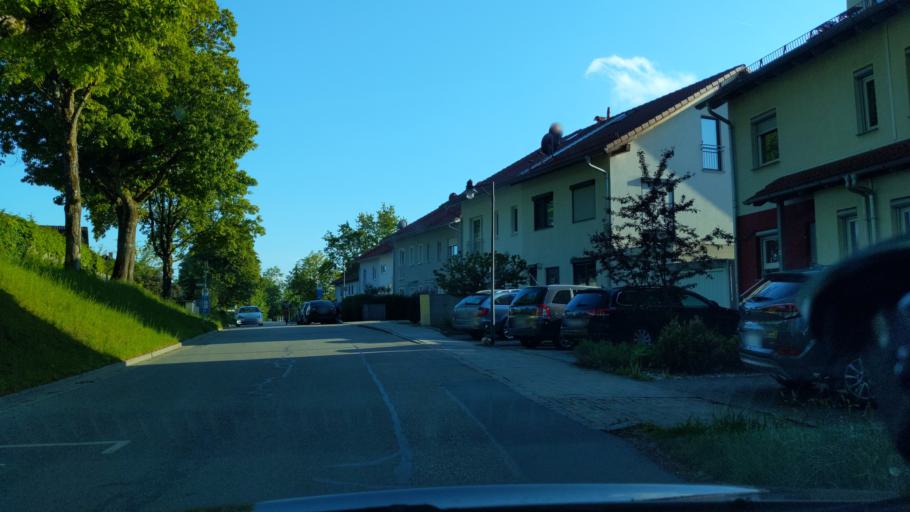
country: DE
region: Bavaria
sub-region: Upper Bavaria
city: Ebersberg
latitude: 48.0728
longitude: 11.9700
